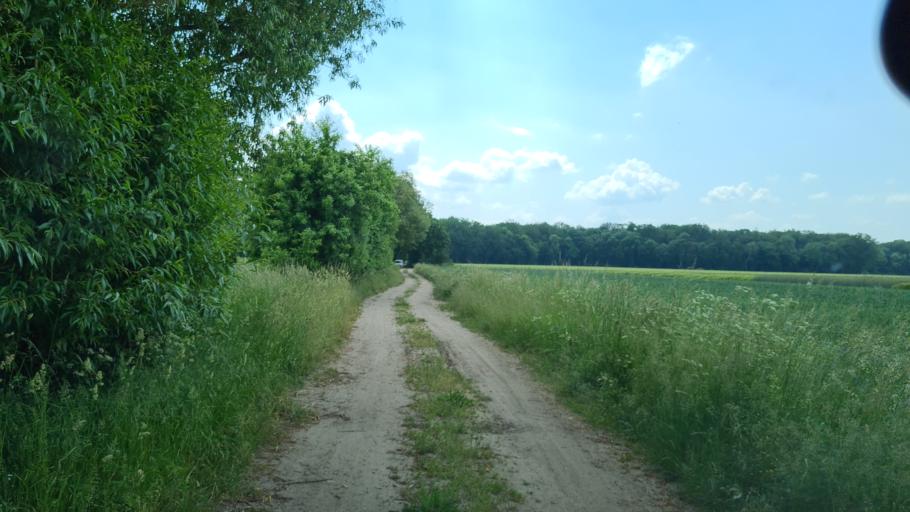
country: DE
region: Brandenburg
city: Sonnewalde
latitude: 51.7075
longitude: 13.6360
